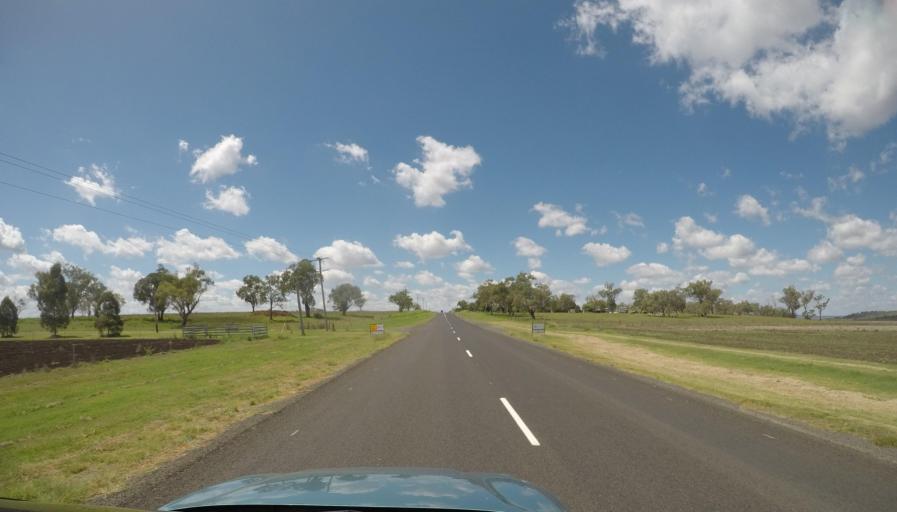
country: AU
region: Queensland
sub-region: Toowoomba
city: Oakey
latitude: -27.5280
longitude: 151.5848
